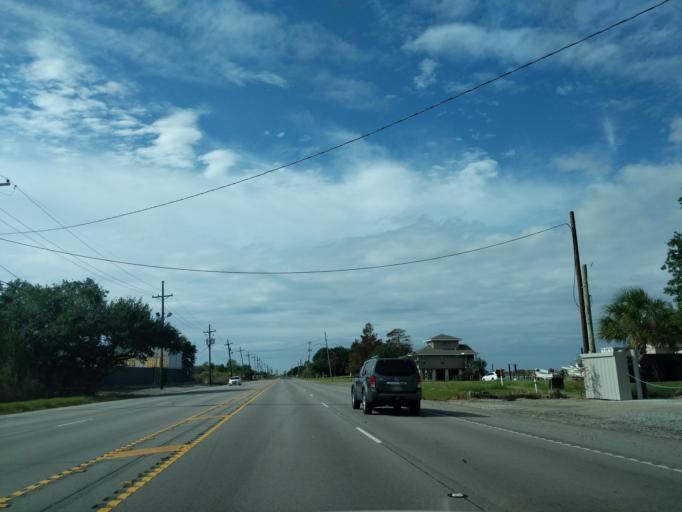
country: US
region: Louisiana
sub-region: Saint Tammany Parish
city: Eden Isle
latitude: 30.0696
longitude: -89.8368
